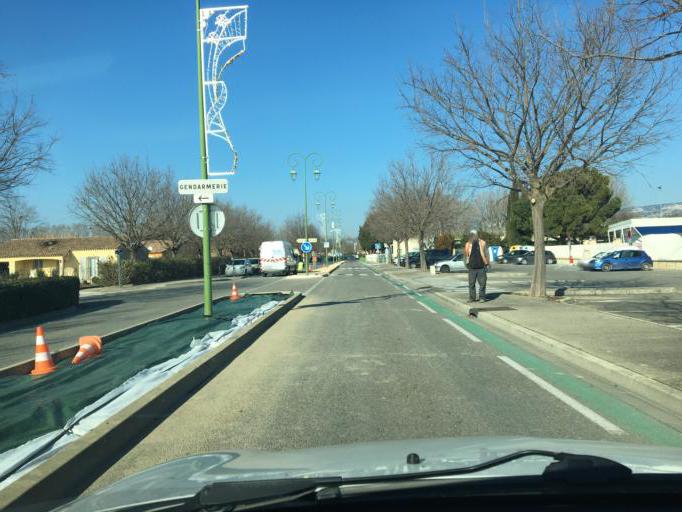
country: FR
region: Provence-Alpes-Cote d'Azur
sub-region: Departement des Bouches-du-Rhone
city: Mallemort
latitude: 43.7237
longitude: 5.1805
